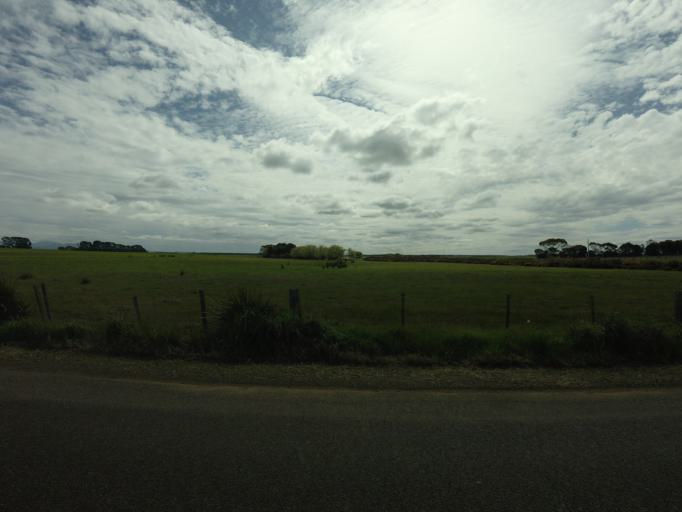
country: AU
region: Tasmania
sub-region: Northern Midlands
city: Longford
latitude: -41.7152
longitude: 147.1906
